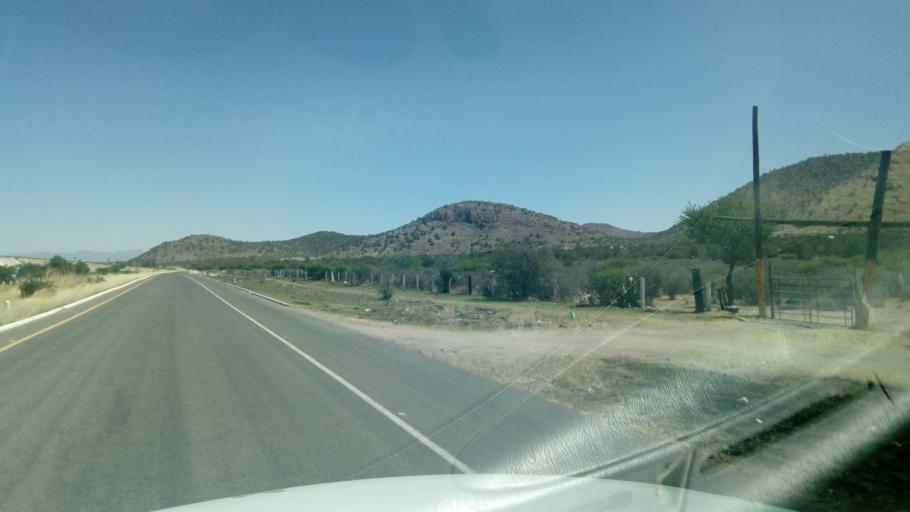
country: MX
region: Durango
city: Victoria de Durango
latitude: 24.1511
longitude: -104.7081
